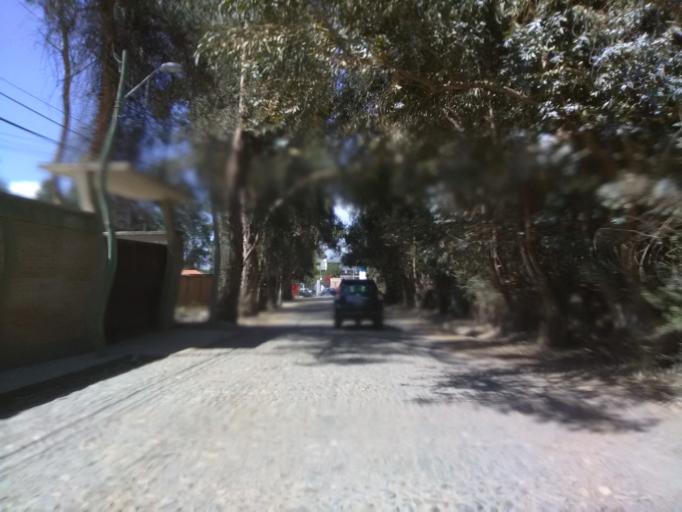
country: BO
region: Cochabamba
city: Cochabamba
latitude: -17.3536
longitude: -66.2011
